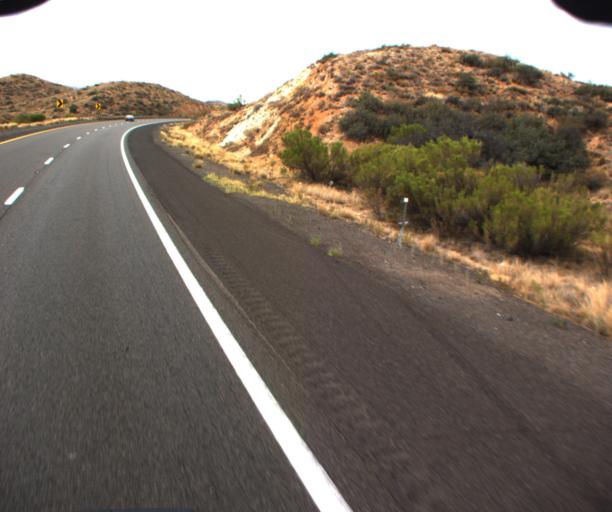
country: US
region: Arizona
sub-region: Yavapai County
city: Cordes Lakes
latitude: 34.2715
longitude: -112.1145
